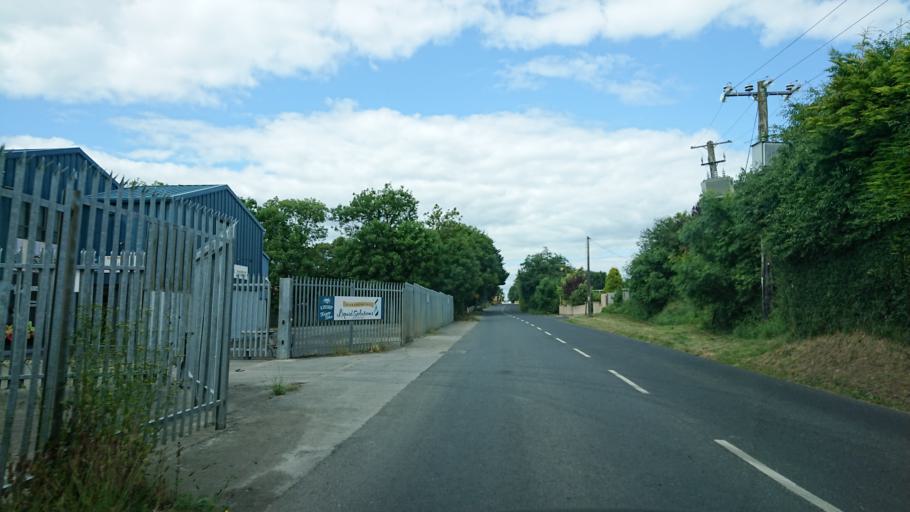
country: IE
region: Munster
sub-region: Waterford
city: Waterford
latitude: 52.2290
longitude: -7.1453
